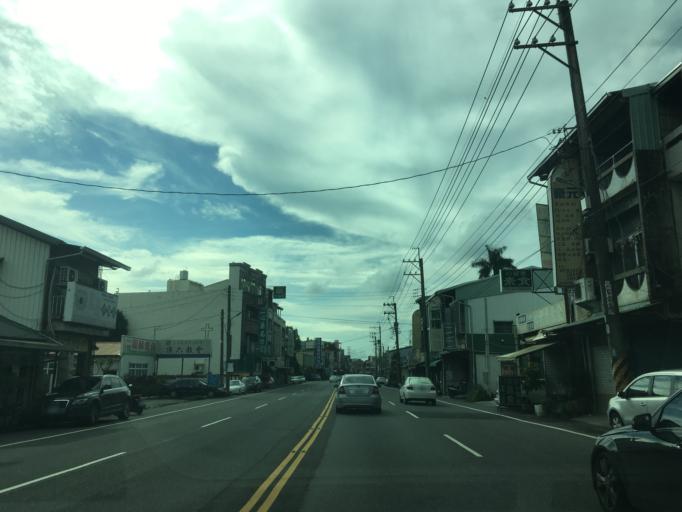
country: TW
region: Taiwan
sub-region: Chiayi
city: Jiayi Shi
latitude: 23.4475
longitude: 120.4921
